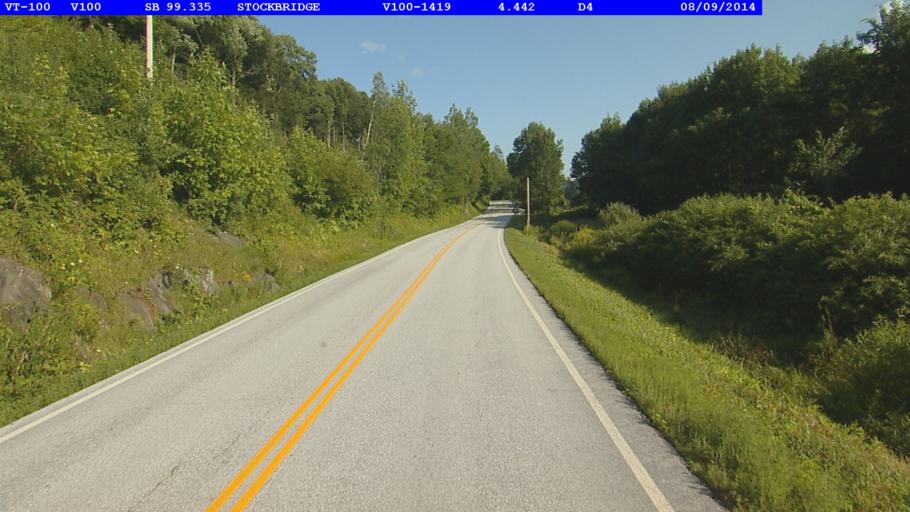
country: US
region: Vermont
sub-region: Orange County
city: Randolph
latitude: 43.8004
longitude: -72.7714
